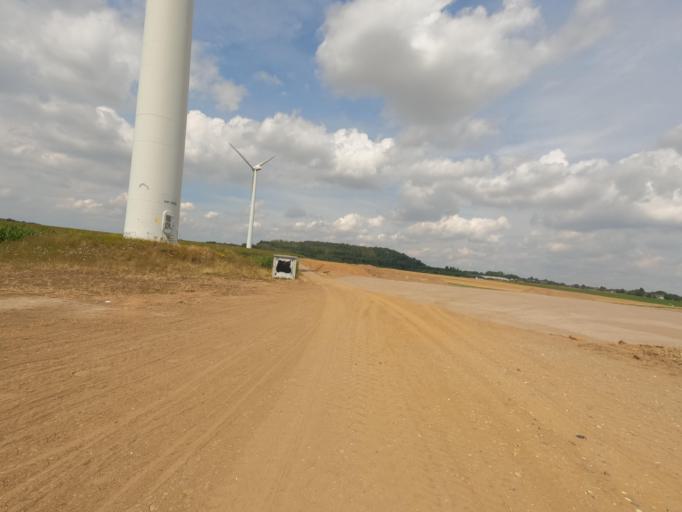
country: DE
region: North Rhine-Westphalia
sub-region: Regierungsbezirk Koln
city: Alsdorf
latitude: 50.8982
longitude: 6.1598
